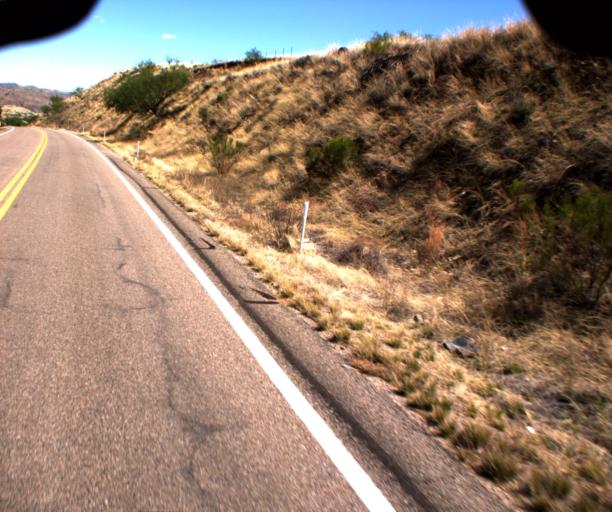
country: US
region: Arizona
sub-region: Santa Cruz County
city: Rio Rico
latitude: 31.4679
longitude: -110.8214
